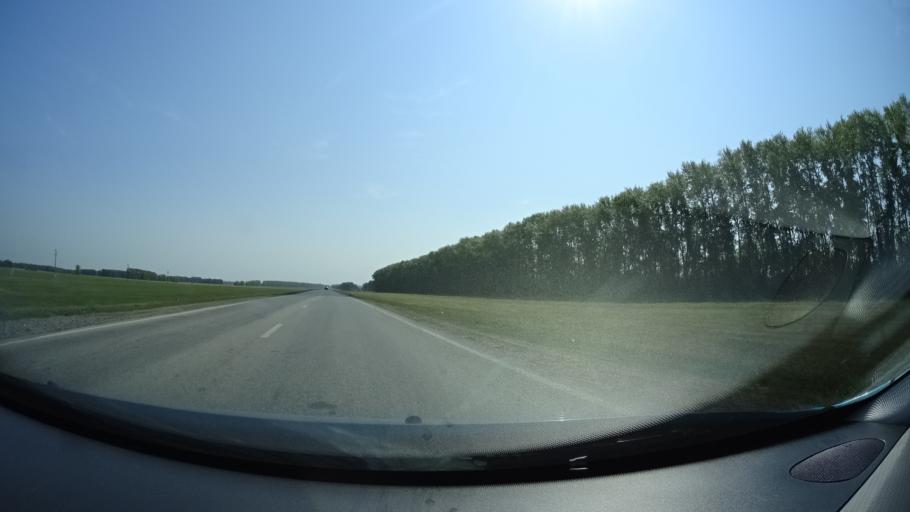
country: RU
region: Bashkortostan
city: Karmaskaly
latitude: 54.4042
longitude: 56.0823
